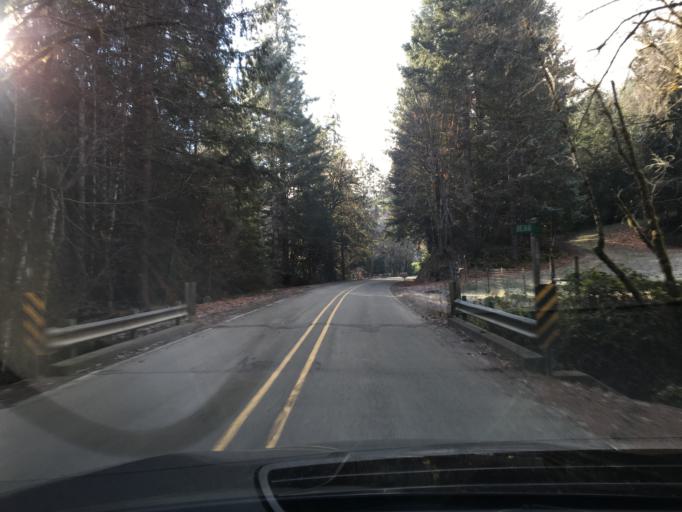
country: US
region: Oregon
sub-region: Douglas County
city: Roseburg
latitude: 43.3393
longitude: -123.5913
